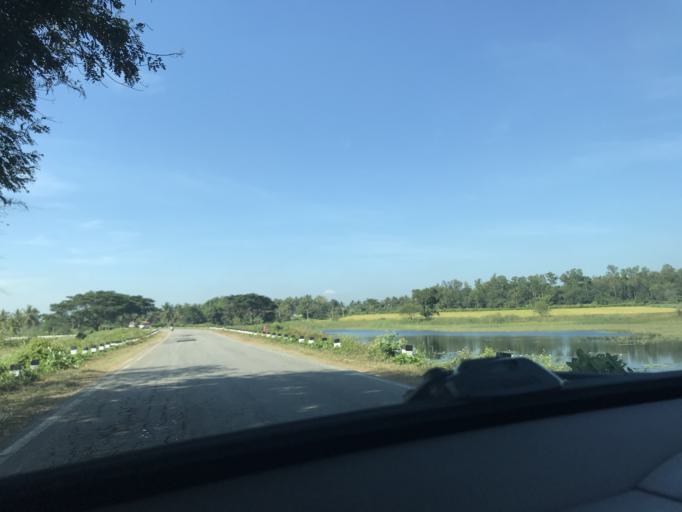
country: IN
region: Karnataka
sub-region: Mysore
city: Heggadadevankote
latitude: 12.1256
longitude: 76.4302
